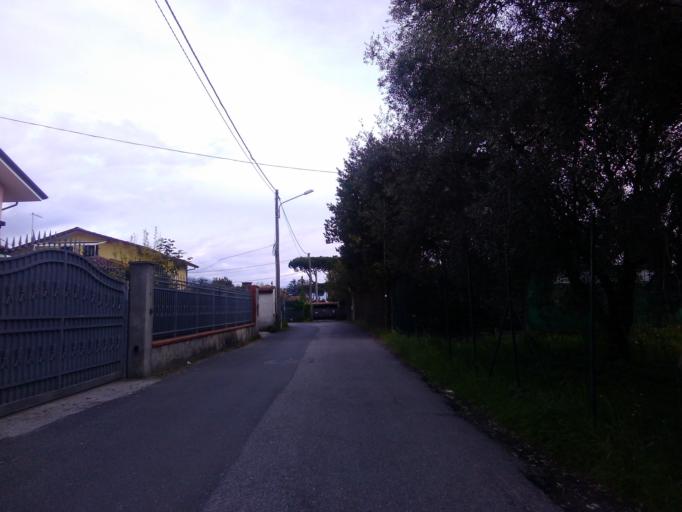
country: IT
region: Tuscany
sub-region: Provincia di Massa-Carrara
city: Marina di Carrara
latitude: 44.0531
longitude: 10.0386
